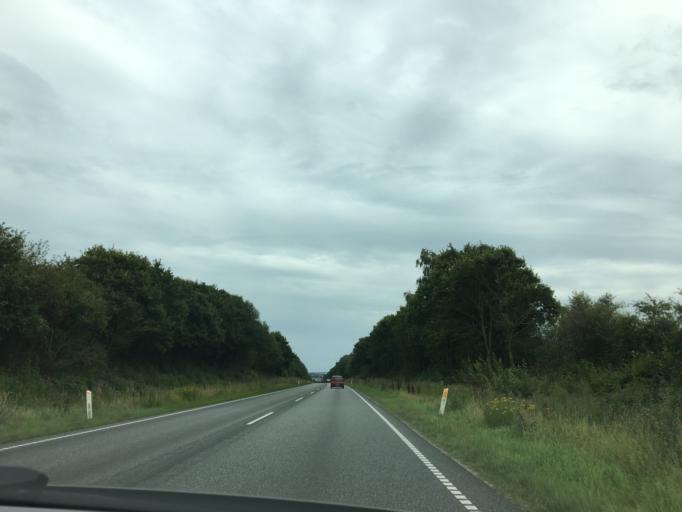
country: DK
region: South Denmark
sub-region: Vejle Kommune
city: Borkop
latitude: 55.6606
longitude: 9.6165
